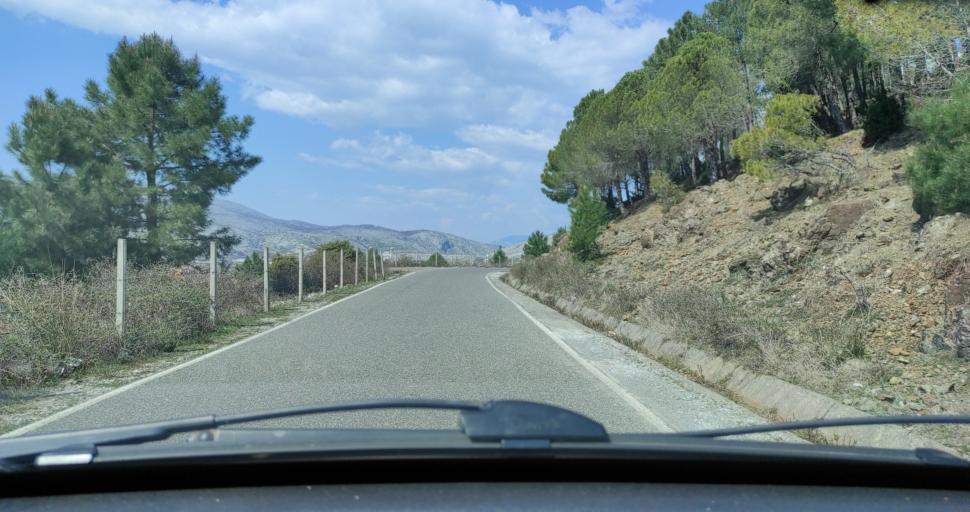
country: AL
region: Shkoder
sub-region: Rrethi i Shkodres
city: Vau i Dejes
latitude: 41.9953
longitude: 19.6494
